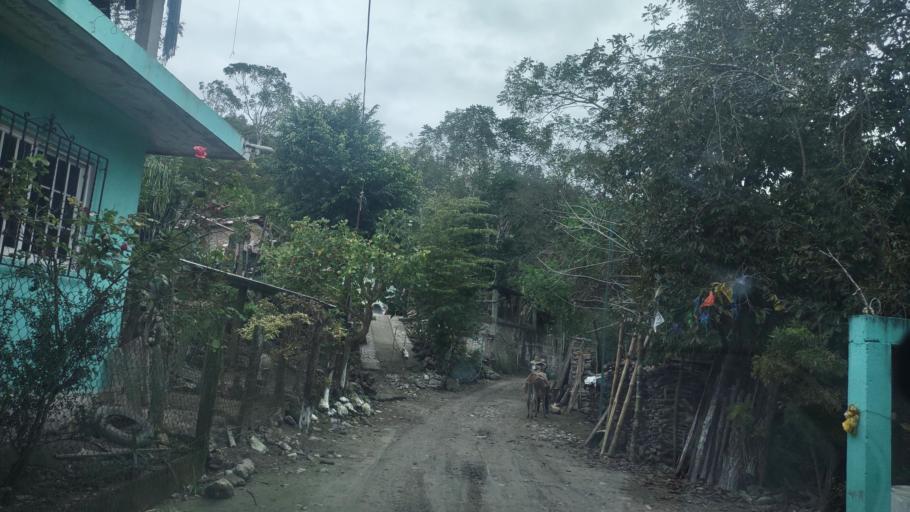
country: MX
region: Veracruz
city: Papantla de Olarte
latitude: 20.4363
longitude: -97.2619
